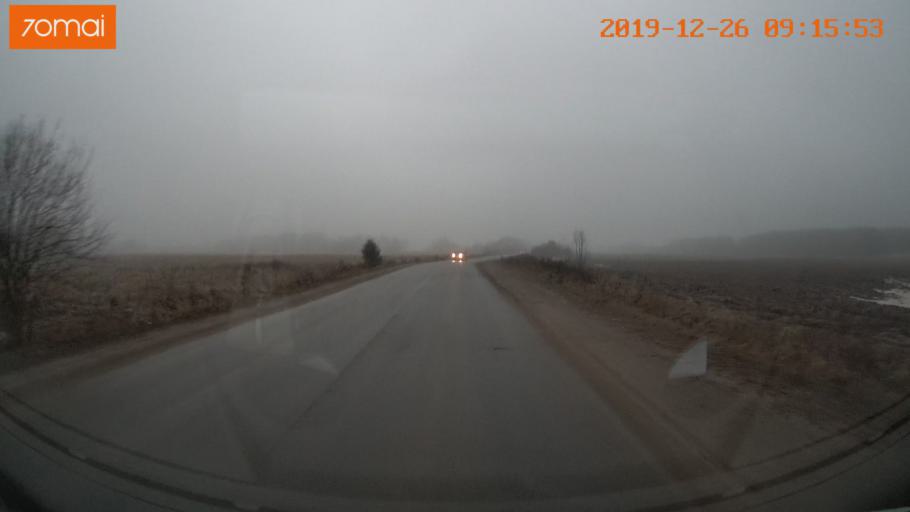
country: RU
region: Vologda
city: Gryazovets
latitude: 58.9109
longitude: 40.2390
